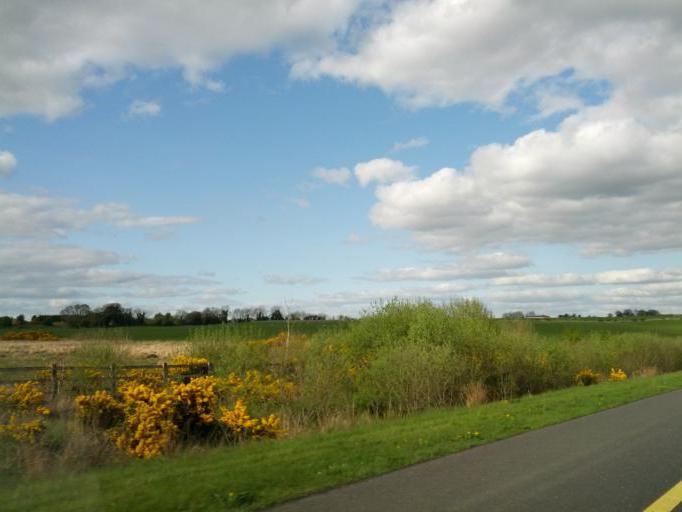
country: IE
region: Connaught
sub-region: County Galway
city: Ballinasloe
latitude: 53.3189
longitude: -8.1559
